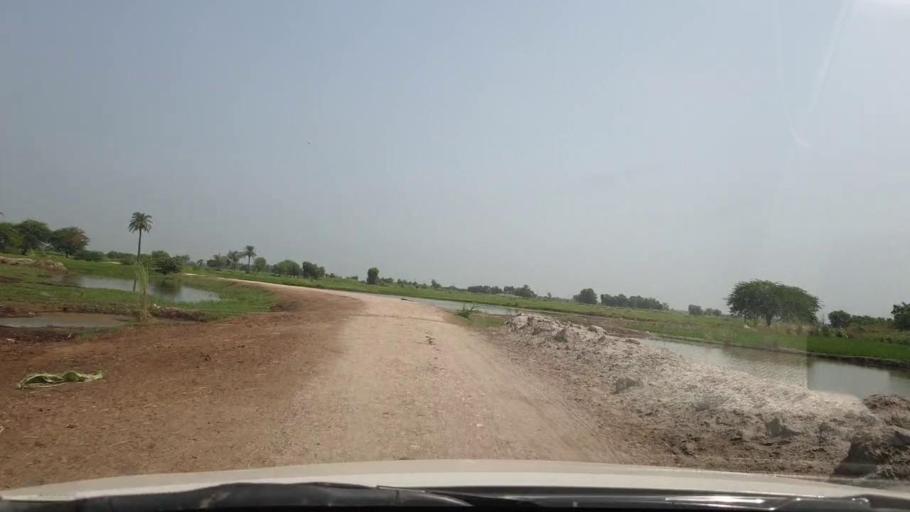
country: PK
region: Sindh
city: Shikarpur
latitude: 27.9590
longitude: 68.7077
